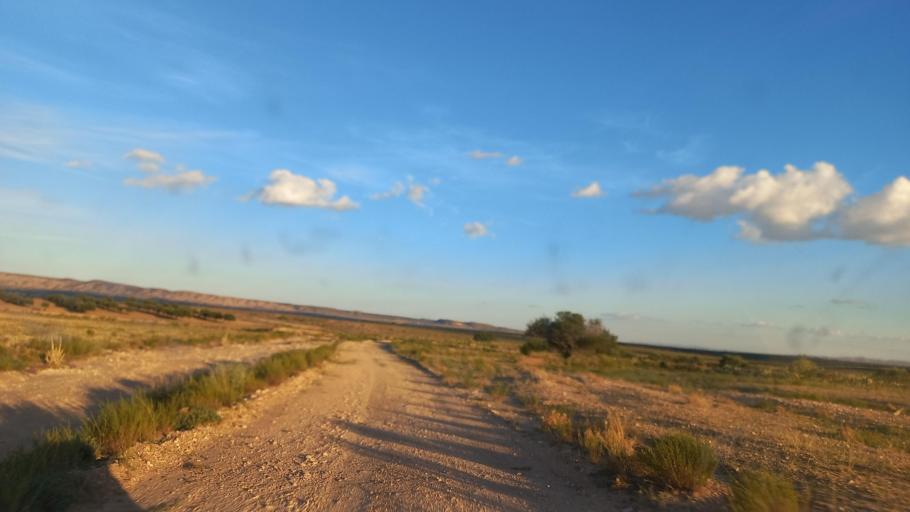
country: TN
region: Al Qasrayn
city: Sbiba
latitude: 35.3485
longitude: 9.0255
